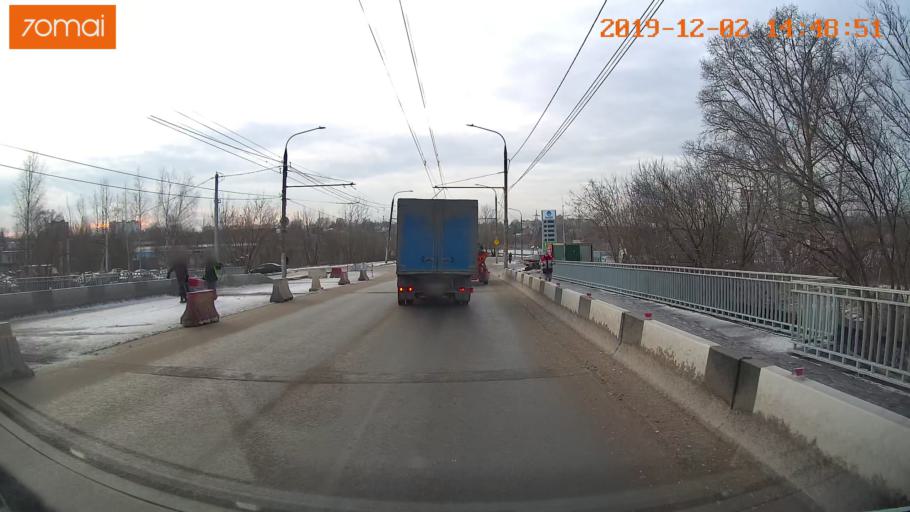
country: RU
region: Ivanovo
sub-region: Gorod Ivanovo
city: Ivanovo
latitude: 56.9842
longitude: 41.0159
